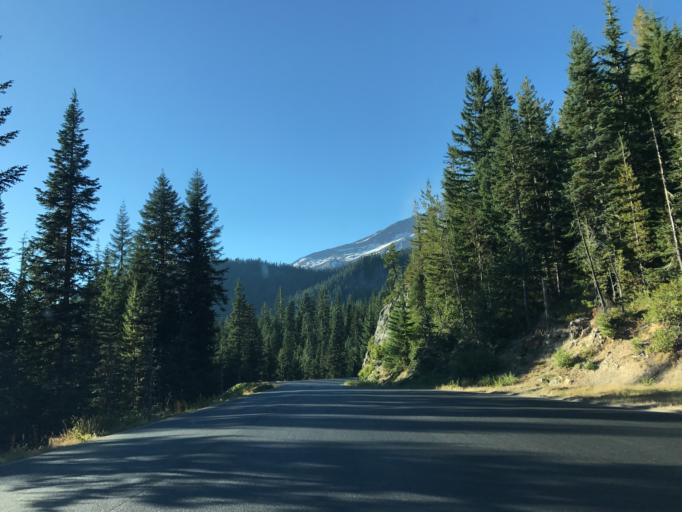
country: US
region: Washington
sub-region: Pierce County
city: Buckley
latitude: 46.7764
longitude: -121.7573
